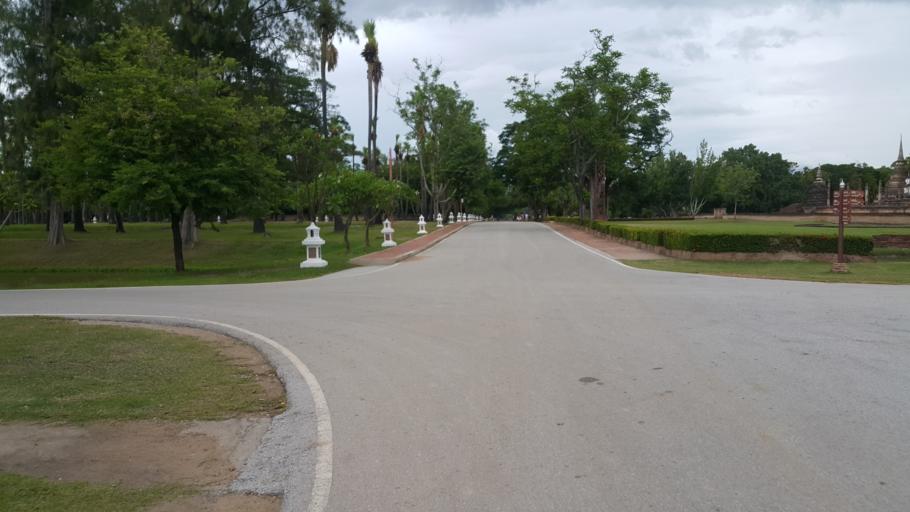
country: TH
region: Sukhothai
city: Ban Na
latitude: 17.0186
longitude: 99.7049
